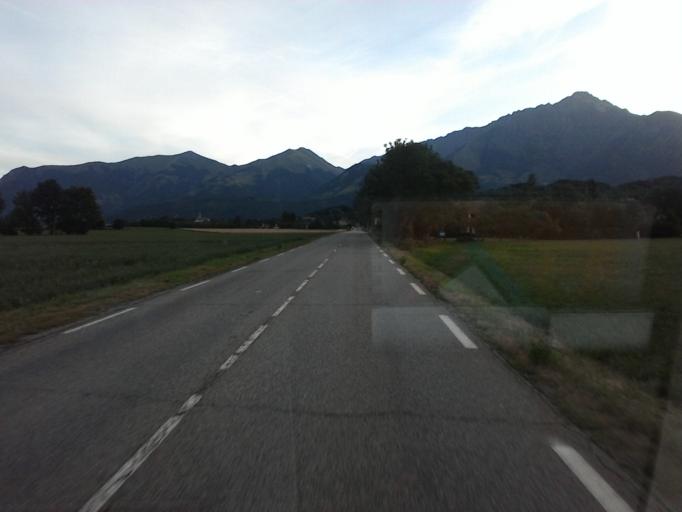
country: FR
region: Provence-Alpes-Cote d'Azur
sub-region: Departement des Hautes-Alpes
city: Saint-Bonnet-en-Champsaur
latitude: 44.7464
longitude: 6.0080
